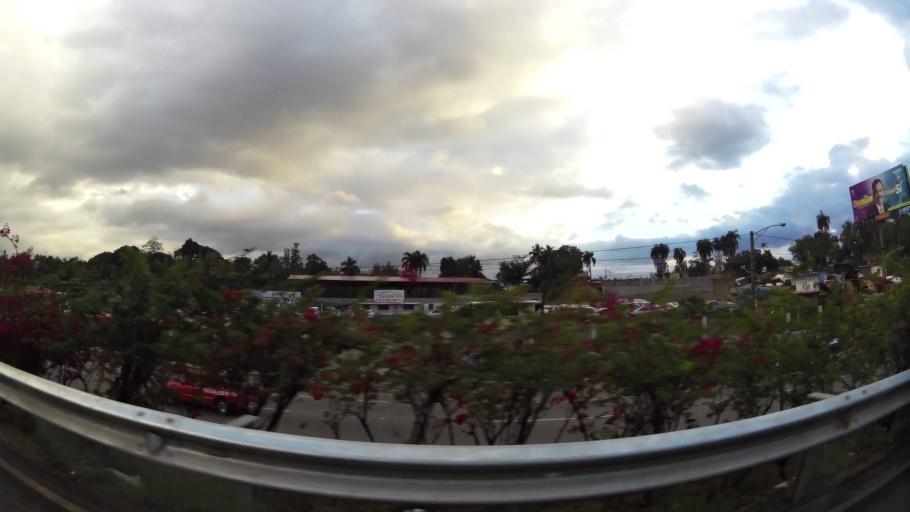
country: DO
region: Santo Domingo
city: Santo Domingo Oeste
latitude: 18.5373
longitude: -70.0208
